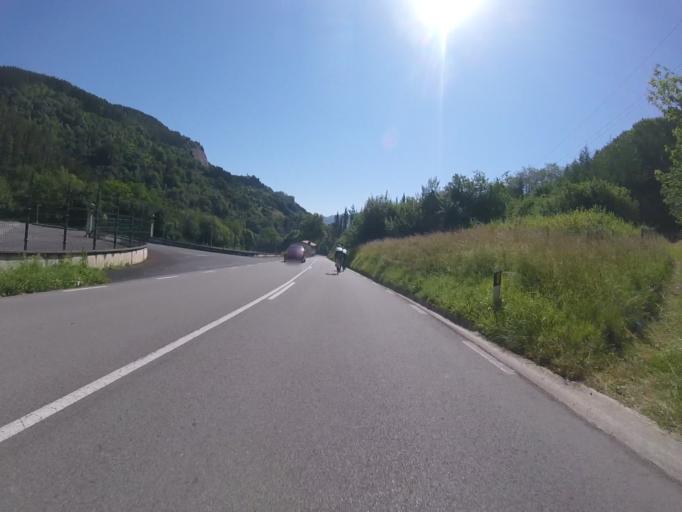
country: ES
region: Basque Country
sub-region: Provincia de Guipuzcoa
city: Albiztur
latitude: 43.1245
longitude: -2.1153
